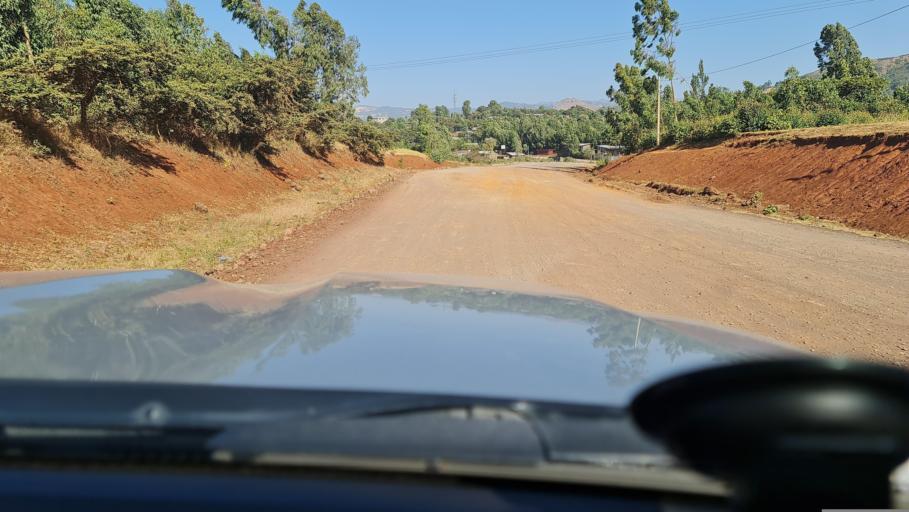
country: ET
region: Oromiya
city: Waliso
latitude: 8.6021
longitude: 37.9281
